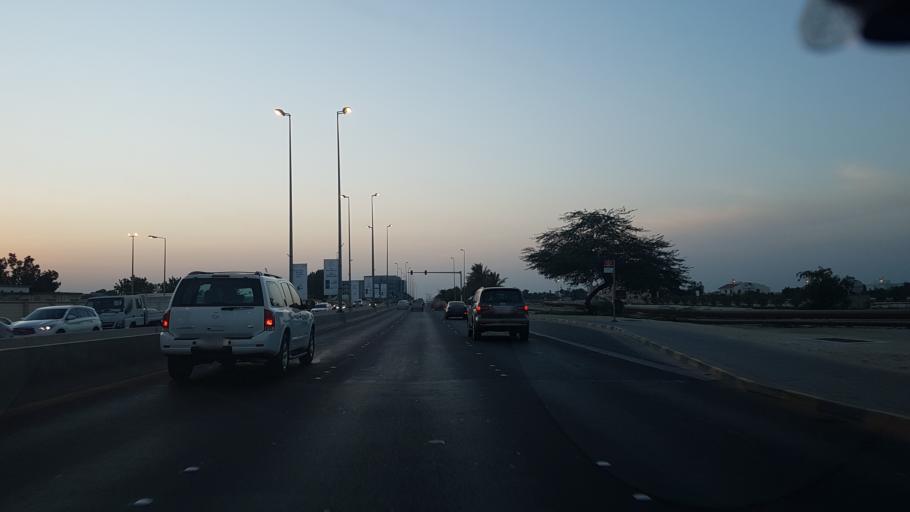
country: BH
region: Northern
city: Ar Rifa'
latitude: 26.1349
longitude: 50.5342
